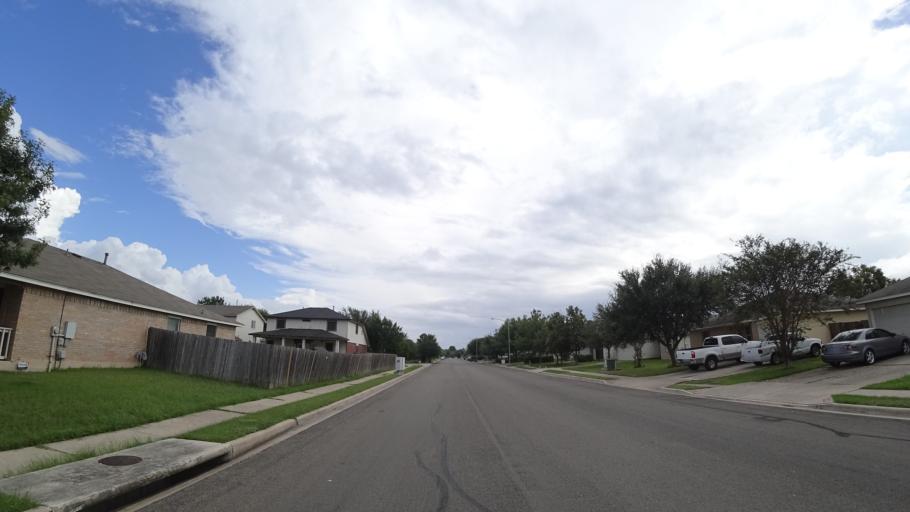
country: US
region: Texas
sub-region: Travis County
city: Onion Creek
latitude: 30.1548
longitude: -97.7410
